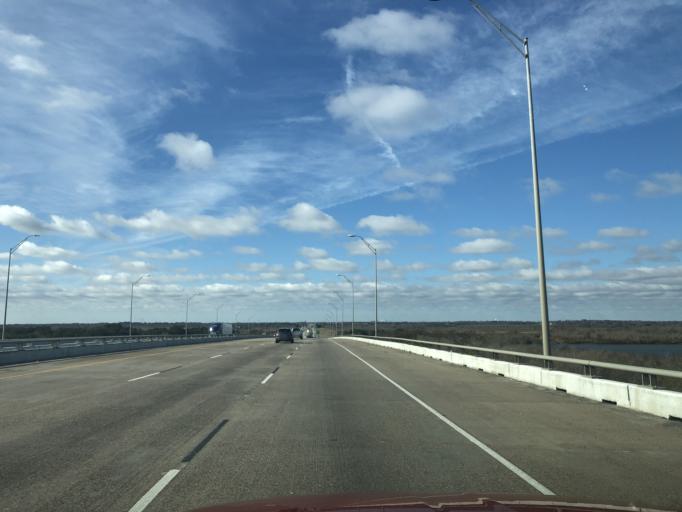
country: US
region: Texas
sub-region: Chambers County
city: Old River-Winfree
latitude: 29.8378
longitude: -94.7639
